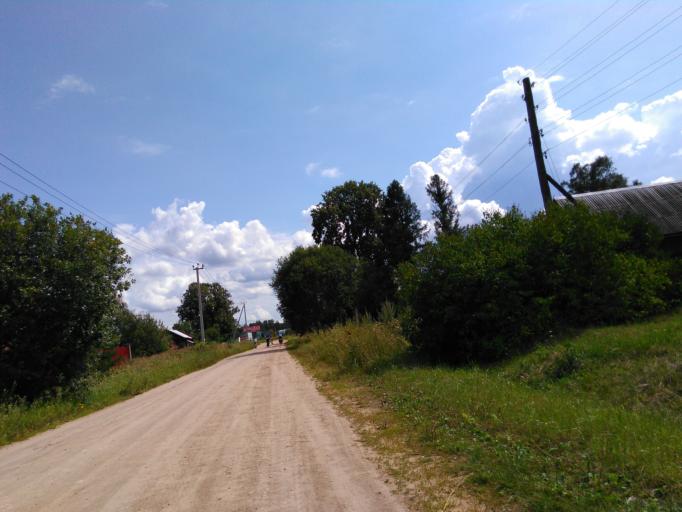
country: RU
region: Vladimir
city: Krasnyy Oktyabr'
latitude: 55.9978
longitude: 38.8547
